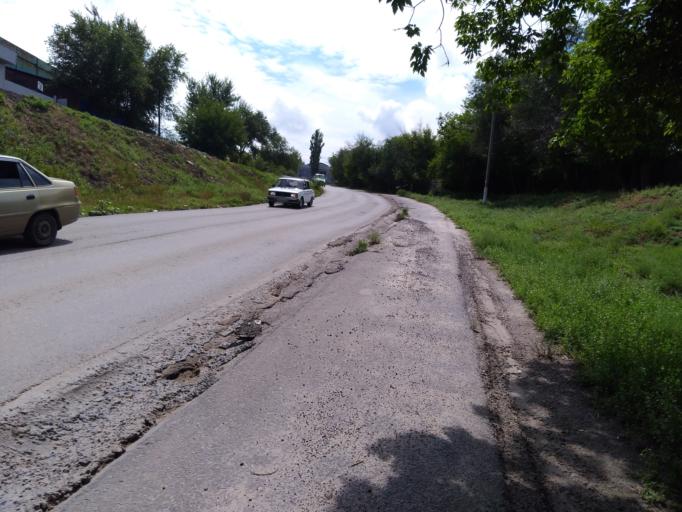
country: RU
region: Volgograd
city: Volgograd
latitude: 48.7118
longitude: 44.4658
